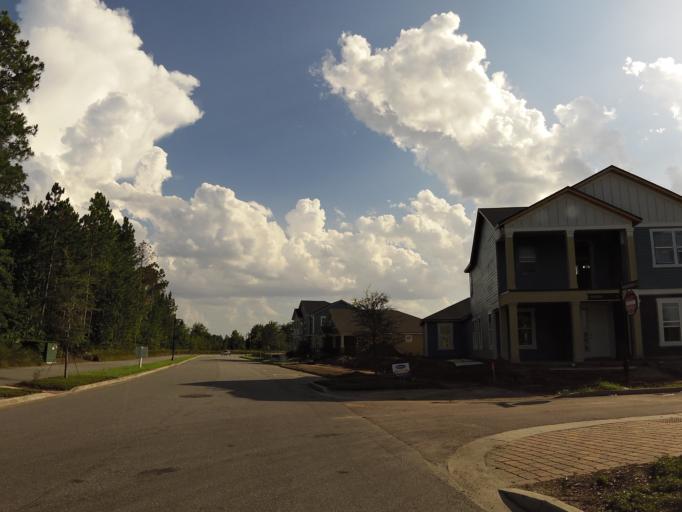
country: US
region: Florida
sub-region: Clay County
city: Green Cove Springs
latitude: 30.0287
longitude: -81.6269
